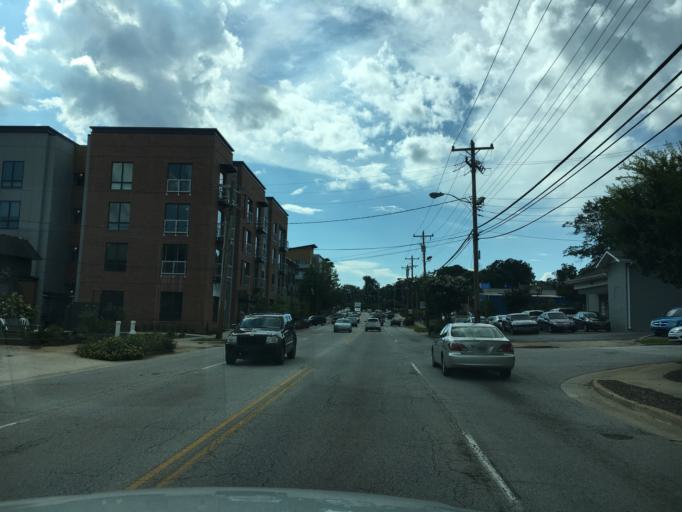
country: US
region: South Carolina
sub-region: Greenville County
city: Greenville
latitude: 34.8609
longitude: -82.3917
